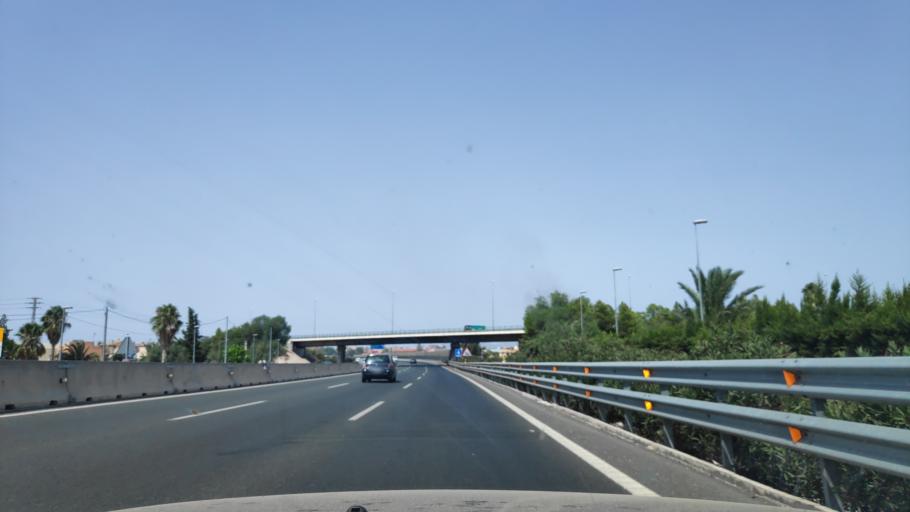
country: ES
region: Murcia
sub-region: Murcia
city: Murcia
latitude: 37.9566
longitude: -1.1371
